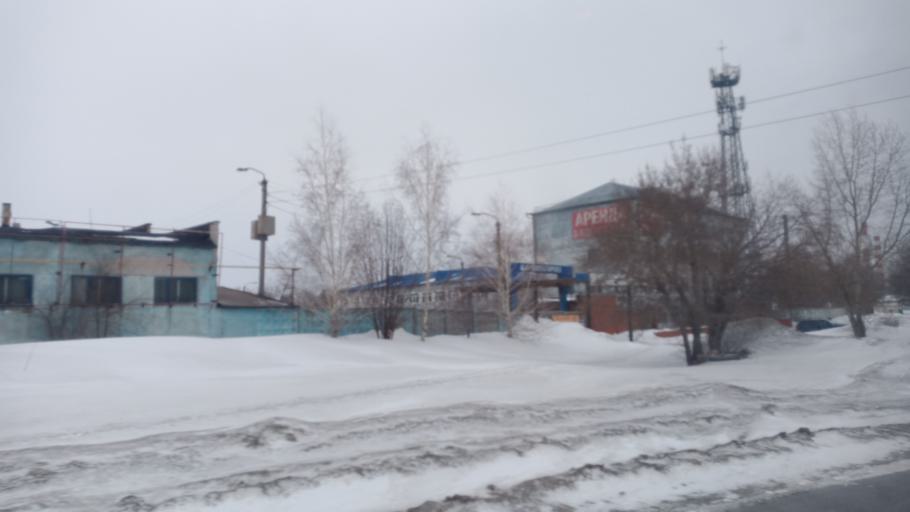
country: RU
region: Altai Krai
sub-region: Gorod Barnaulskiy
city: Barnaul
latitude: 53.3900
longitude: 83.6763
